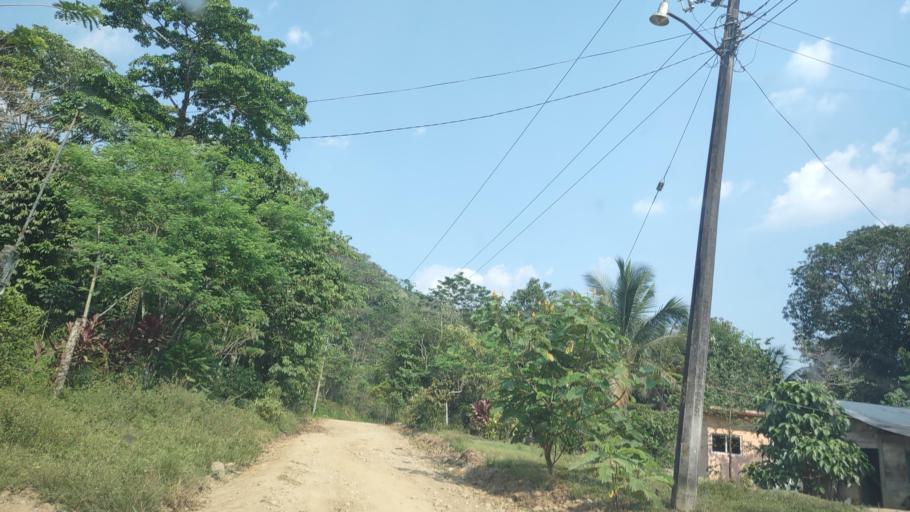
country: MX
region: Chiapas
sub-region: Tecpatan
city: Raudales Malpaso
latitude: 17.3227
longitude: -93.7443
